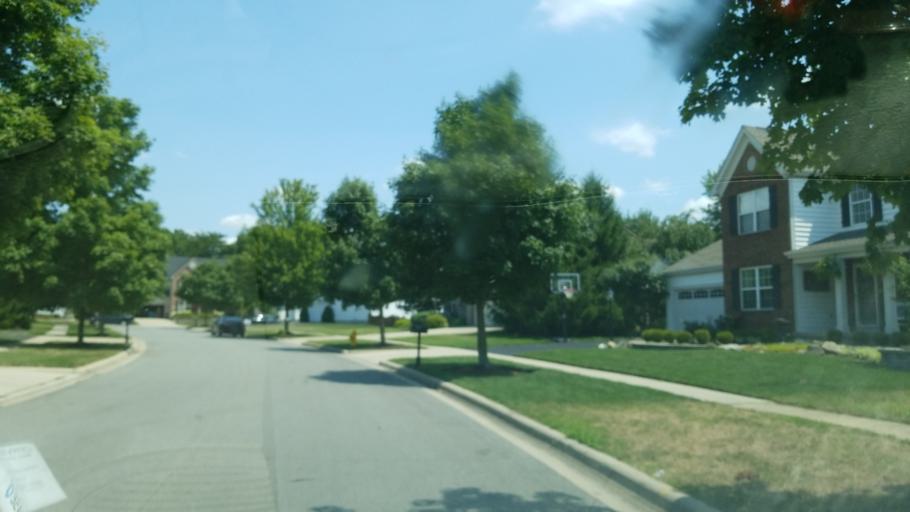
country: US
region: Ohio
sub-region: Delaware County
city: Powell
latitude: 40.1945
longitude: -83.1296
